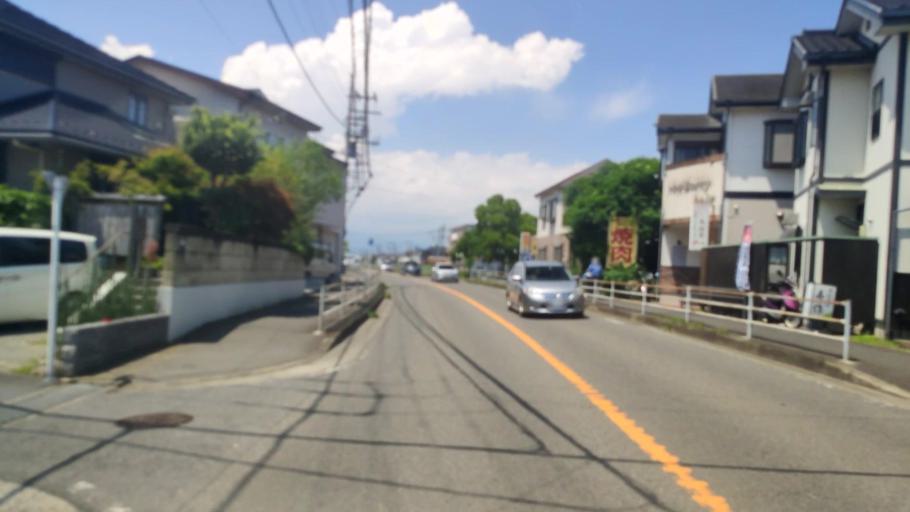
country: JP
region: Kanagawa
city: Hiratsuka
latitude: 35.3382
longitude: 139.3099
